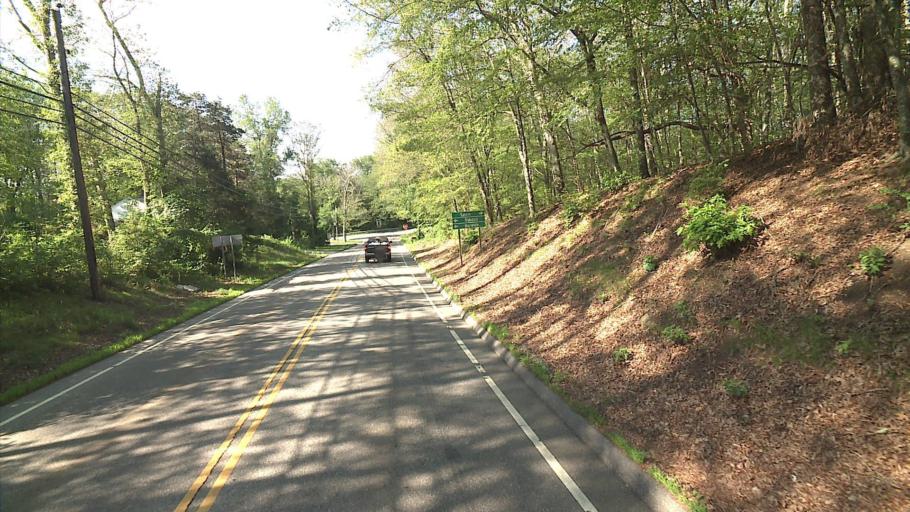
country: US
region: Connecticut
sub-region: New London County
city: Montville Center
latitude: 41.5034
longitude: -72.2035
